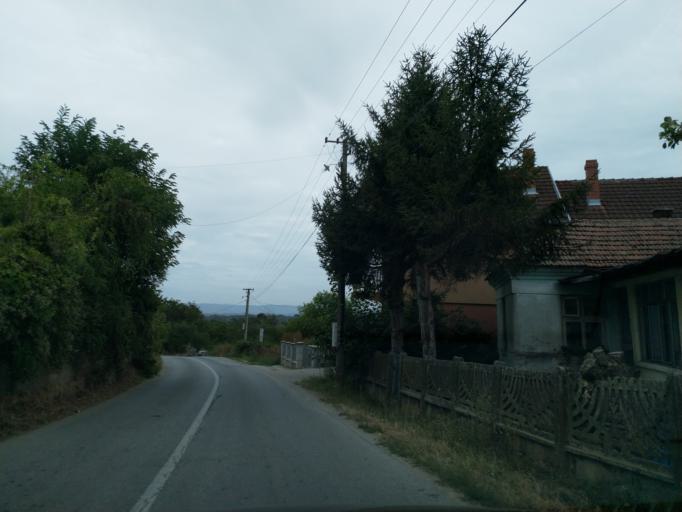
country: RS
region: Central Serbia
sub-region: Pomoravski Okrug
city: Paracin
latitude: 43.8399
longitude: 21.3212
